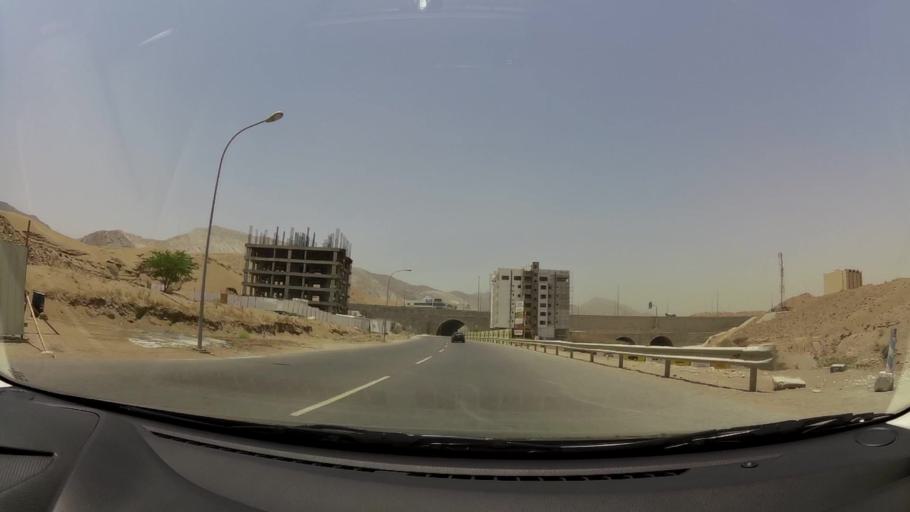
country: OM
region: Muhafazat Masqat
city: Bawshar
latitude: 23.5728
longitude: 58.4159
